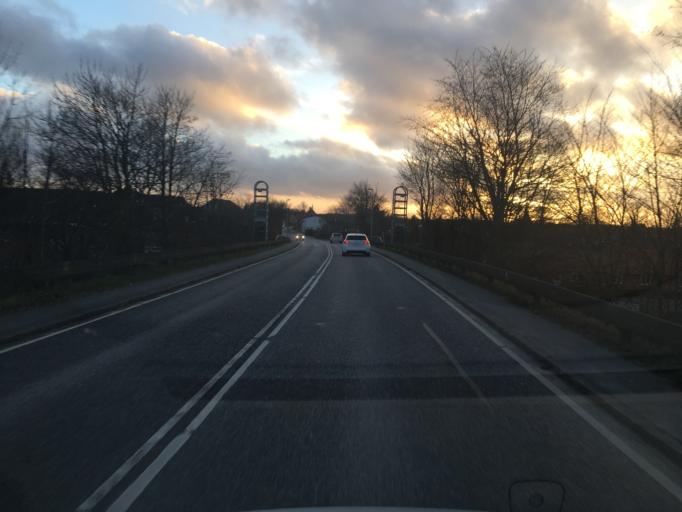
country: DK
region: South Denmark
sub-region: Aabenraa Kommune
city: Tinglev
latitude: 54.9394
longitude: 9.2588
